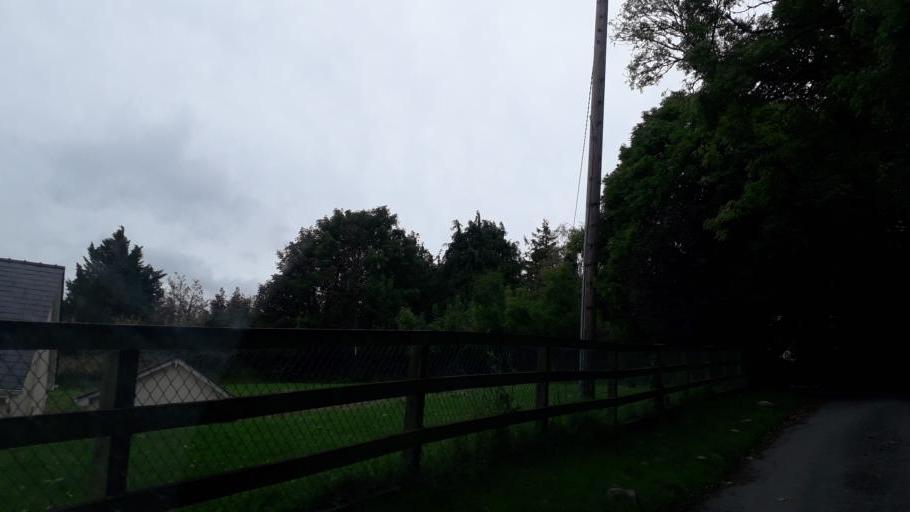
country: IE
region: Leinster
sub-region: Wicklow
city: Enniskerry
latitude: 53.1788
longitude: -6.2113
